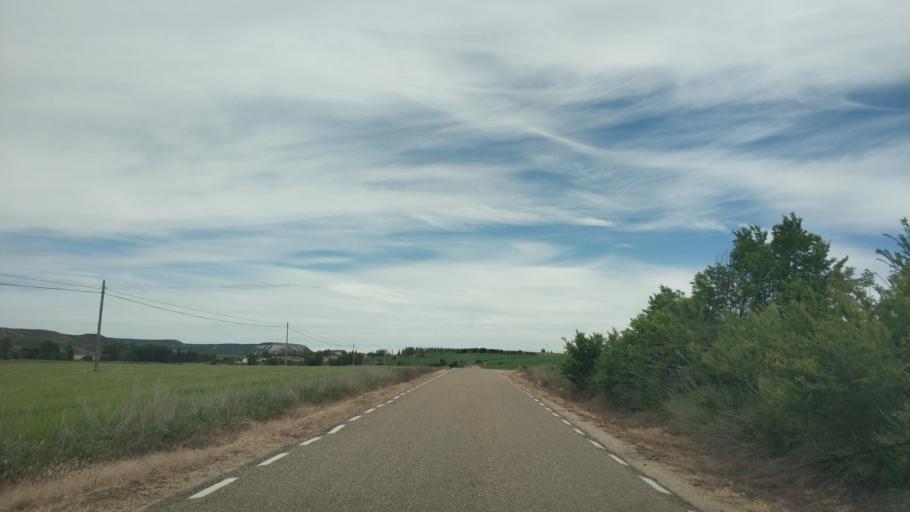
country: ES
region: Castille and Leon
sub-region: Provincia de Soria
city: Berlanga de Duero
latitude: 41.4465
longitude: -2.8341
